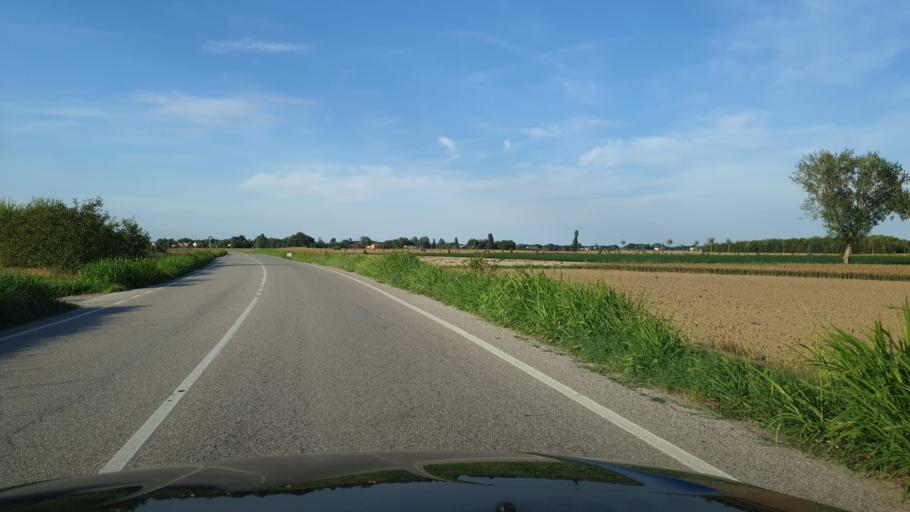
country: IT
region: Veneto
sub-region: Provincia di Rovigo
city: Pincara
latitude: 44.9911
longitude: 11.6142
